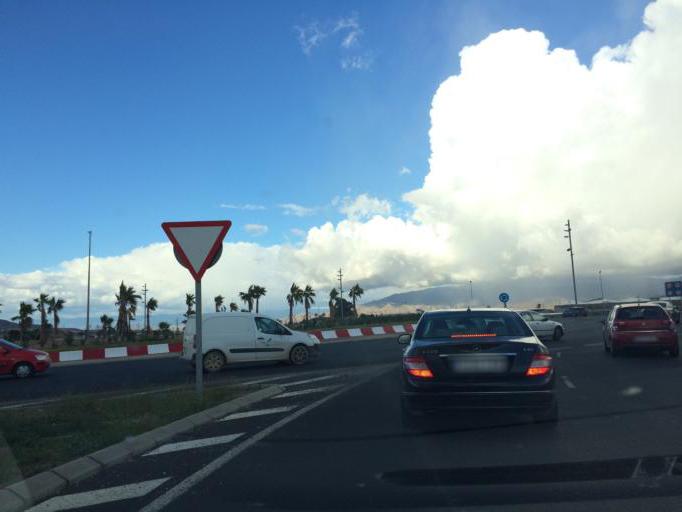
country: ES
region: Andalusia
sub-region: Provincia de Almeria
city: Almeria
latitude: 36.8433
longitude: -2.4207
